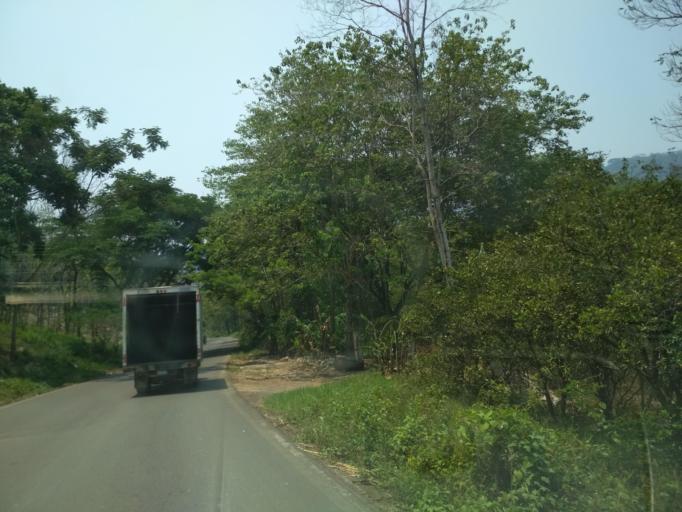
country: MX
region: Veracruz
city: Tezonapa
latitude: 18.6049
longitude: -96.6912
